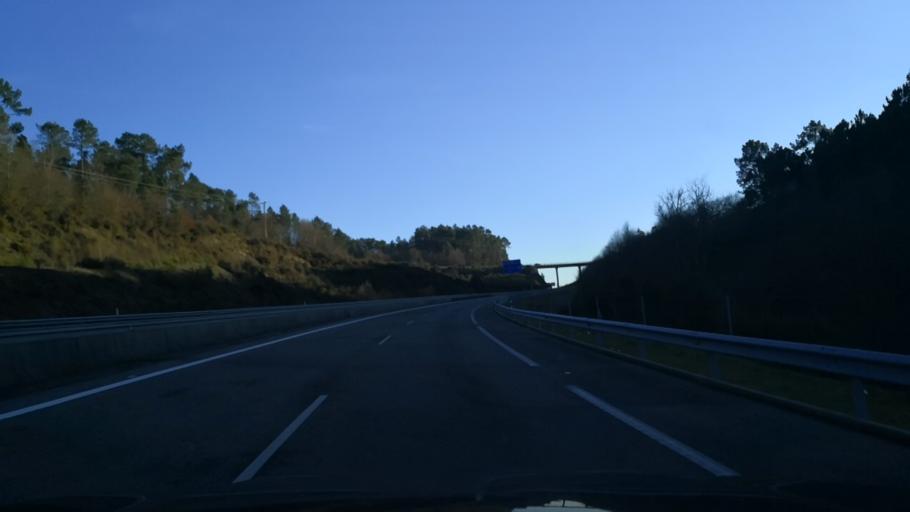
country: ES
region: Galicia
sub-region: Provincia de Ourense
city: Cea
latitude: 42.4577
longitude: -8.0234
